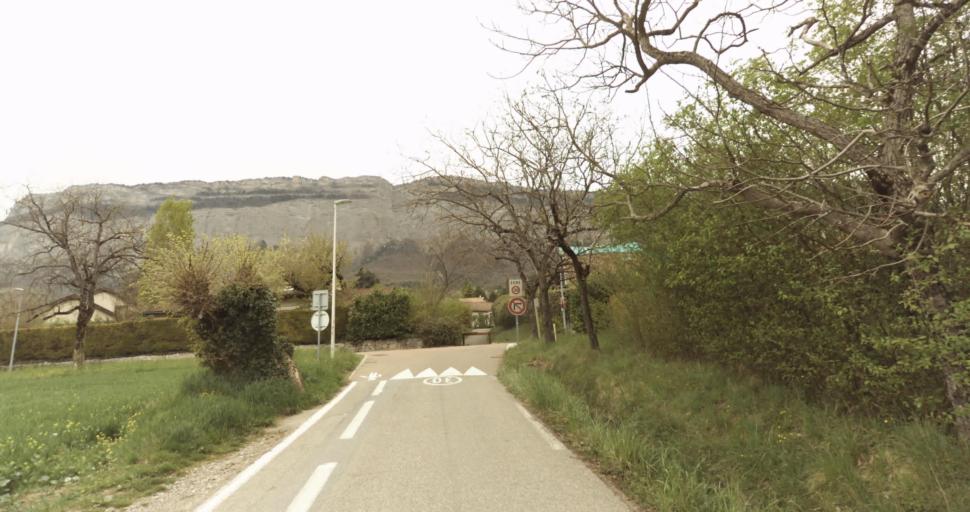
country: FR
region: Rhone-Alpes
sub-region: Departement de l'Isere
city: Biviers
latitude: 45.2317
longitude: 5.8097
